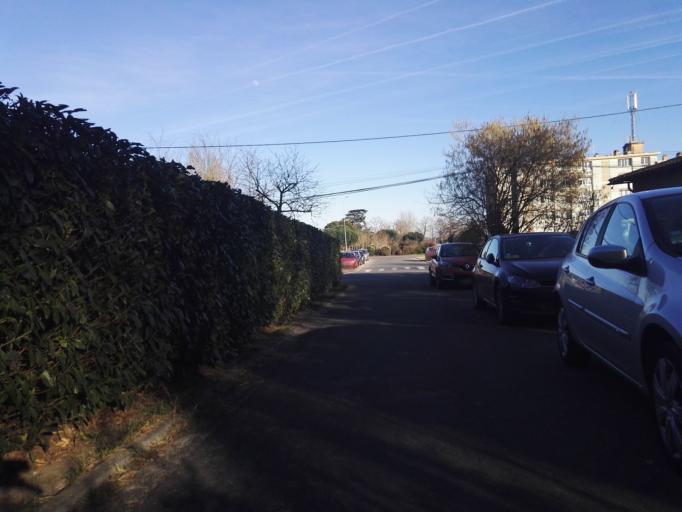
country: FR
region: Aquitaine
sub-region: Departement de la Gironde
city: Pessac
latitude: 44.8160
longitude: -0.6404
